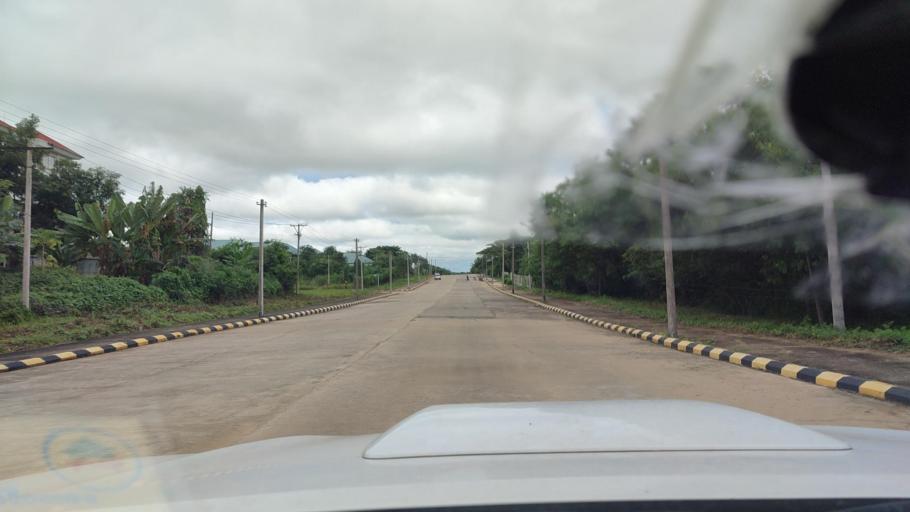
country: MM
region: Mandalay
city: Nay Pyi Taw
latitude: 19.7375
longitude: 96.0630
